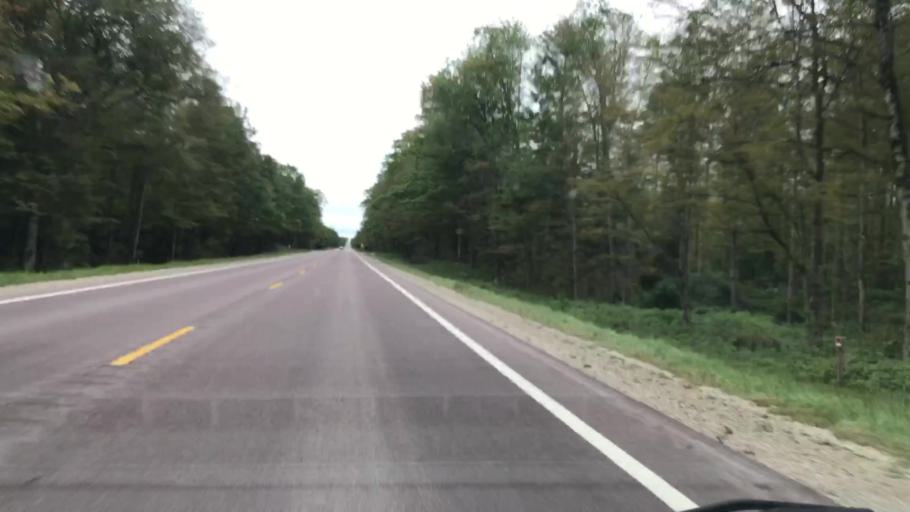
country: US
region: Michigan
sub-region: Luce County
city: Newberry
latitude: 46.2489
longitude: -85.5724
